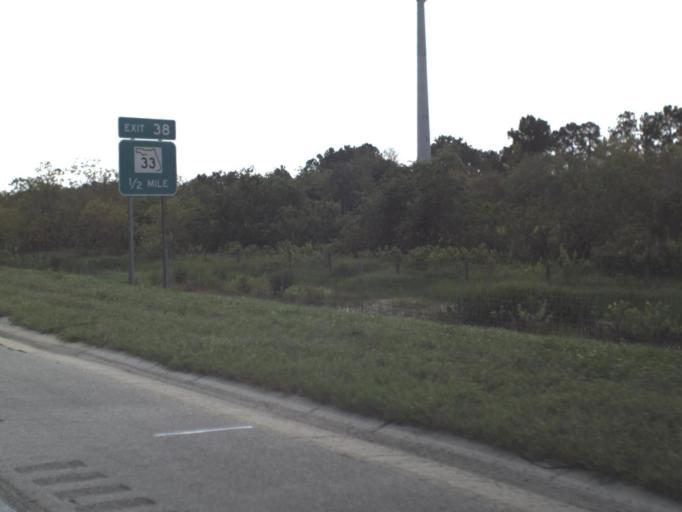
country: US
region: Florida
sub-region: Polk County
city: Gibsonia
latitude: 28.1358
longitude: -81.9112
